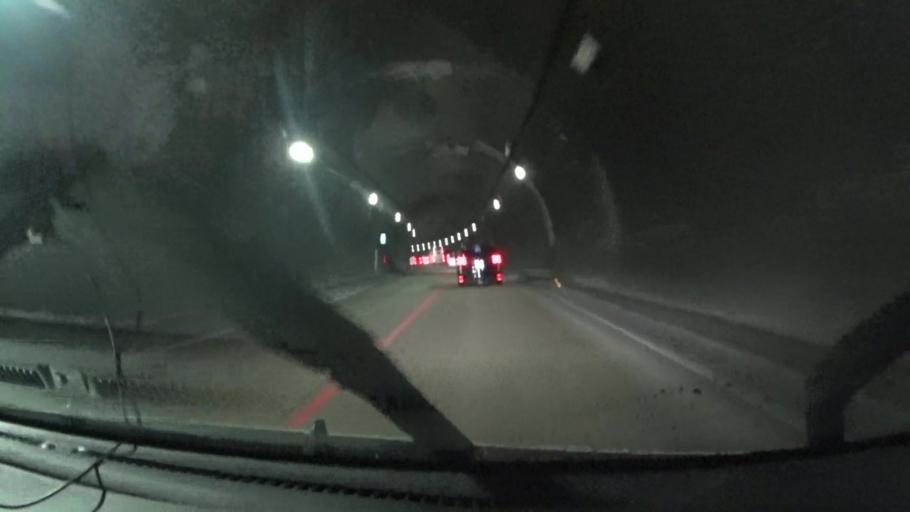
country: JP
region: Kyoto
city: Kameoka
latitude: 34.9962
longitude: 135.5745
